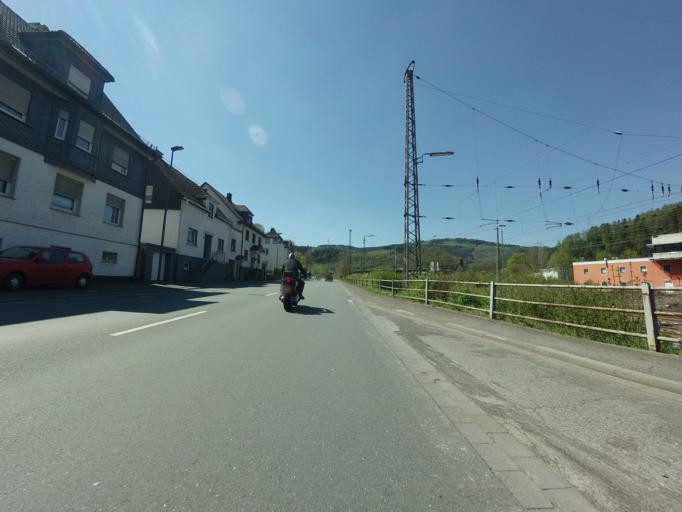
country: DE
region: North Rhine-Westphalia
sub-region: Regierungsbezirk Arnsberg
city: Lennestadt
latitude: 51.0974
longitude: 8.0681
